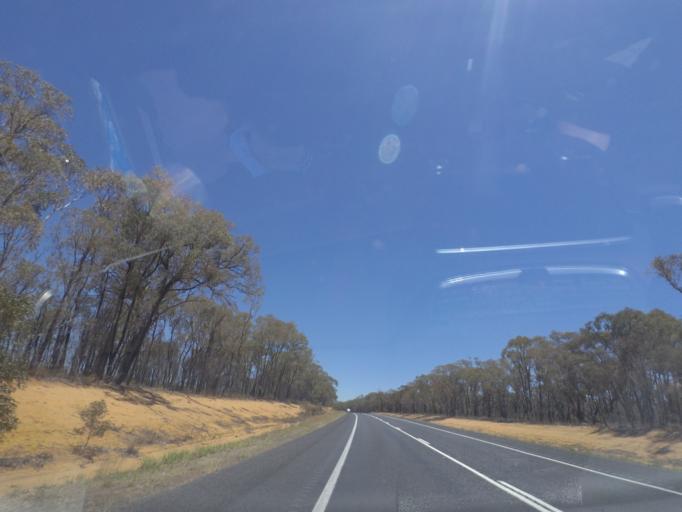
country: AU
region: New South Wales
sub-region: Warrumbungle Shire
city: Coonabarabran
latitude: -31.2040
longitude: 149.3368
